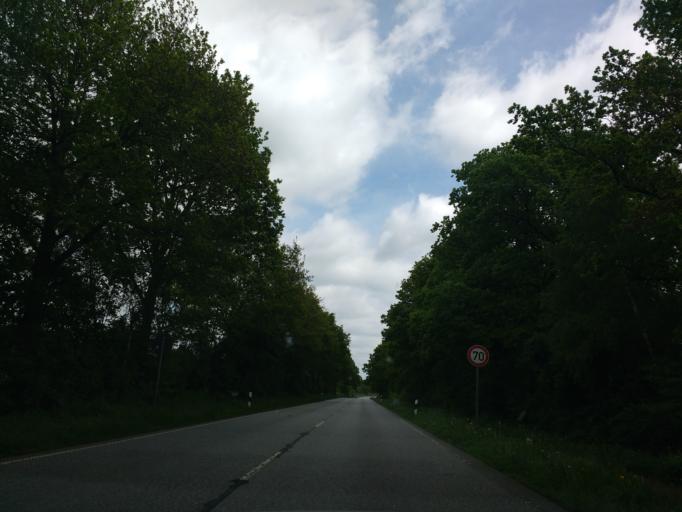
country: DE
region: Schleswig-Holstein
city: Glinde
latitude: 53.5682
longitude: 10.2122
